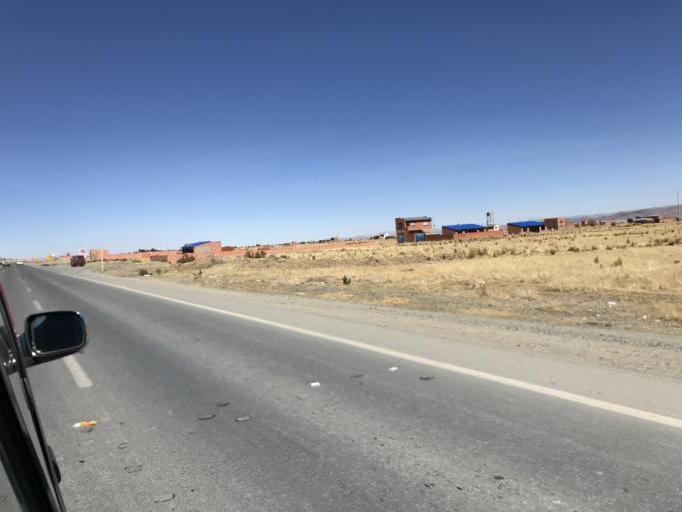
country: BO
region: La Paz
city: Batallas
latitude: -16.3378
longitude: -68.4137
